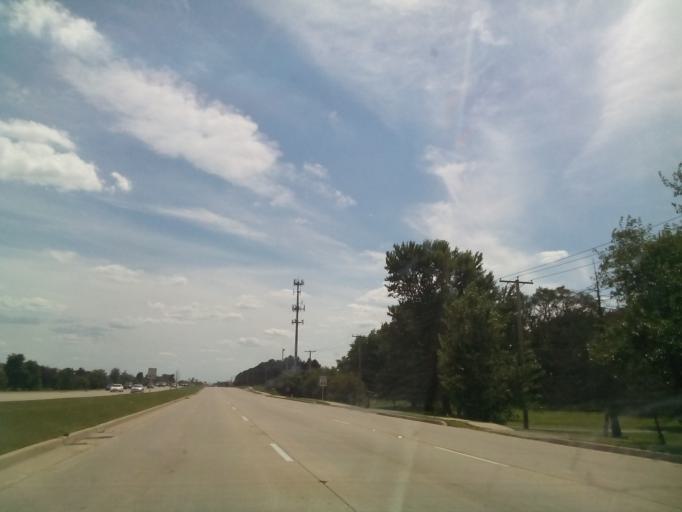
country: US
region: Illinois
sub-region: DuPage County
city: Naperville
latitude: 41.7226
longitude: -88.2062
